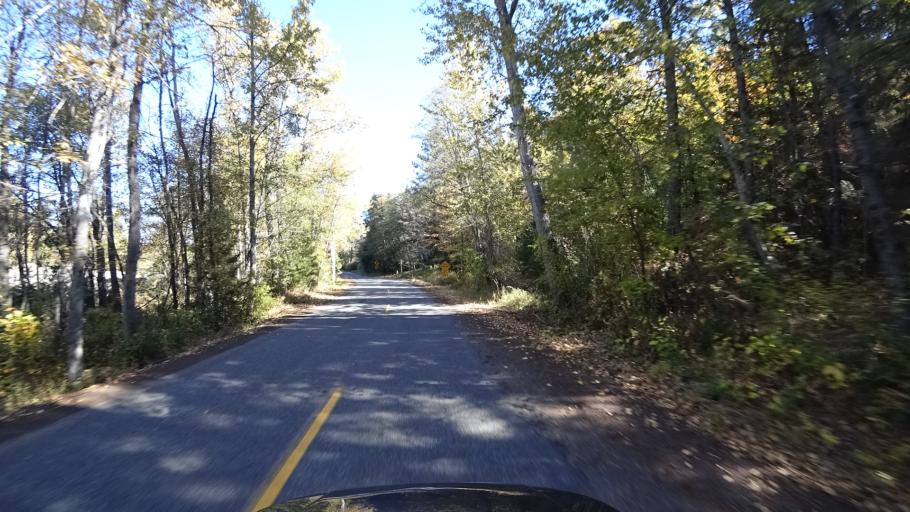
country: US
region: California
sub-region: Siskiyou County
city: Yreka
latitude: 41.5362
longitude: -122.9333
